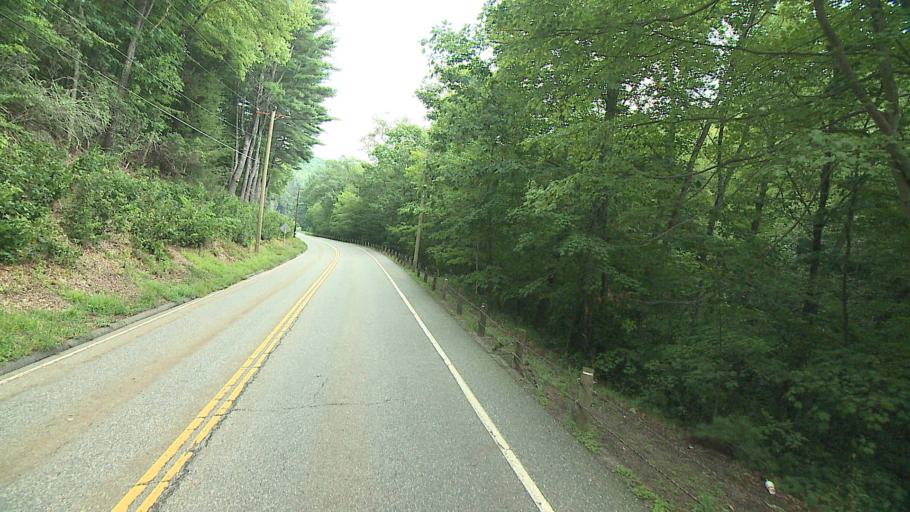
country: US
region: Connecticut
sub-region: Litchfield County
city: Bethlehem Village
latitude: 41.6729
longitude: -73.1470
